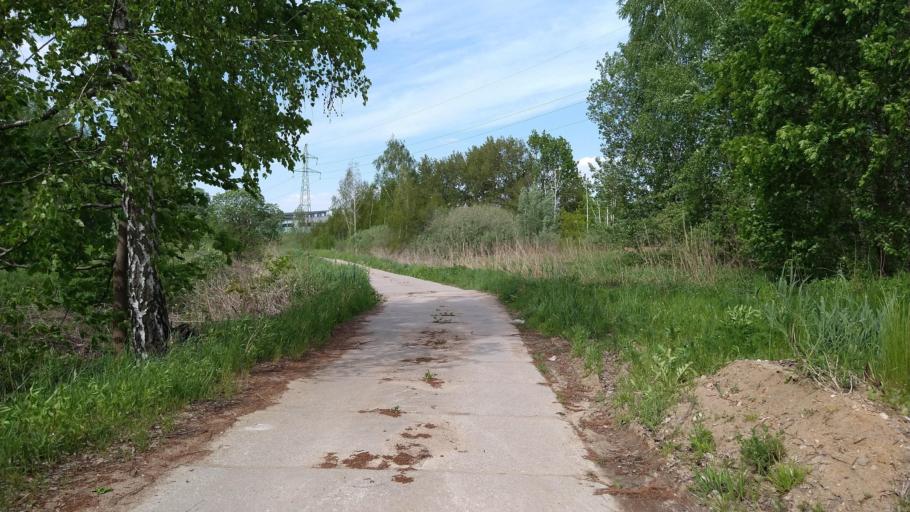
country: PL
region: Warmian-Masurian Voivodeship
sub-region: Powiat olsztynski
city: Olsztyn
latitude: 53.7855
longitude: 20.5512
